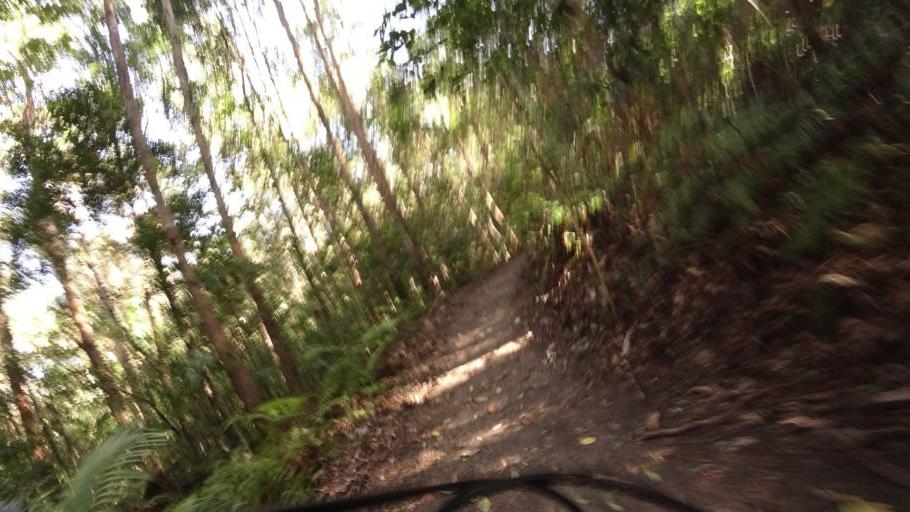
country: AU
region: Queensland
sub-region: Moreton Bay
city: Highvale
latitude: -27.4037
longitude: 152.8011
